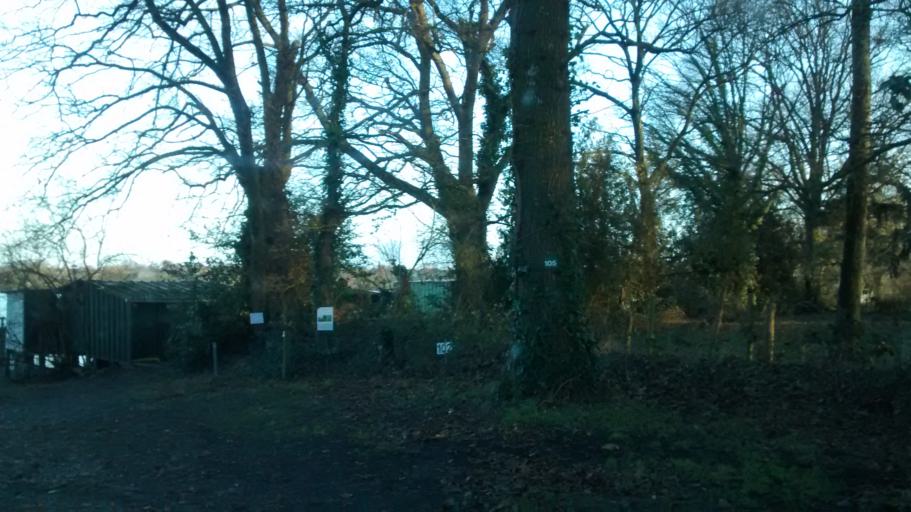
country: FR
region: Brittany
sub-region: Departement d'Ille-et-Vilaine
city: Domalain
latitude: 47.9660
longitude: -1.2526
